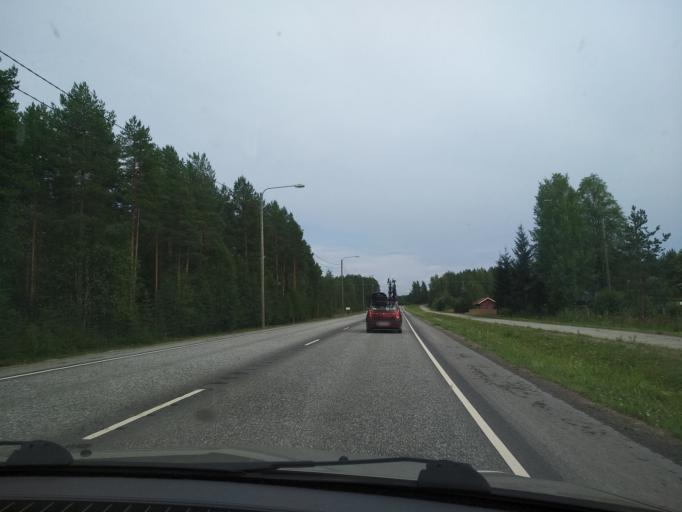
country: FI
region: Kainuu
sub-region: Kajaani
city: Paltamo
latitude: 64.4037
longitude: 27.8637
